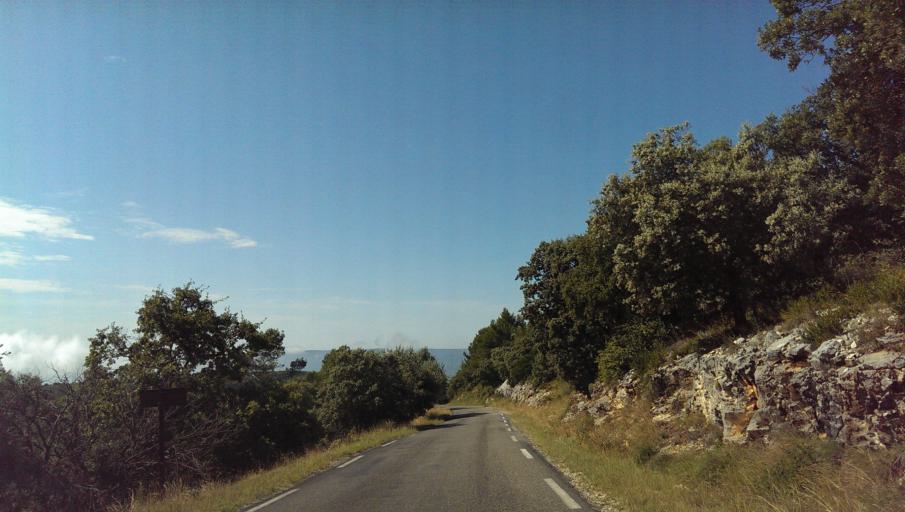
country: FR
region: Provence-Alpes-Cote d'Azur
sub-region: Departement du Vaucluse
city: Gordes
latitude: 43.9487
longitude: 5.1956
